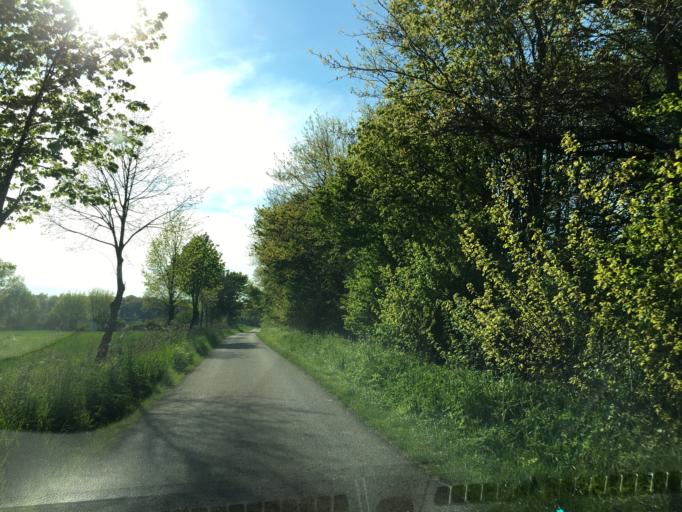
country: DE
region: North Rhine-Westphalia
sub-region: Regierungsbezirk Munster
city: Nordkirchen
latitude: 51.7530
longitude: 7.5146
